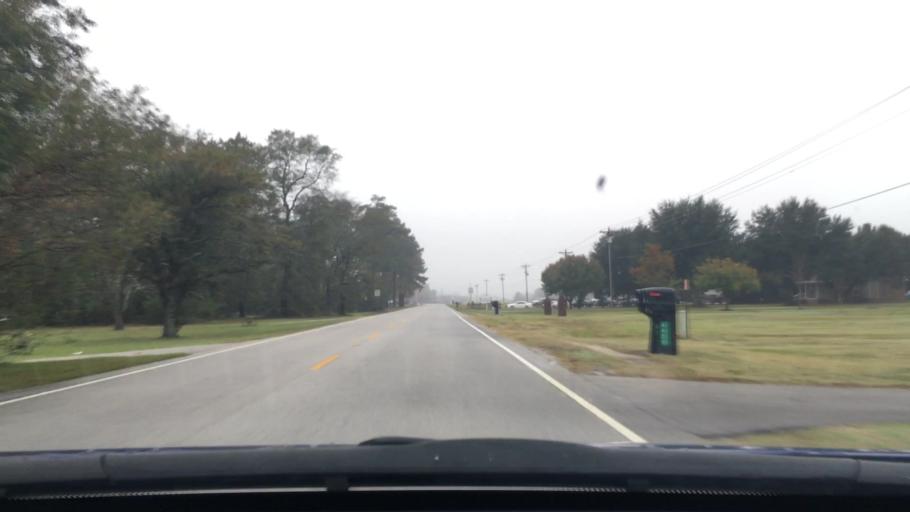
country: US
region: South Carolina
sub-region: Florence County
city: Timmonsville
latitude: 34.2128
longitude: -80.0180
